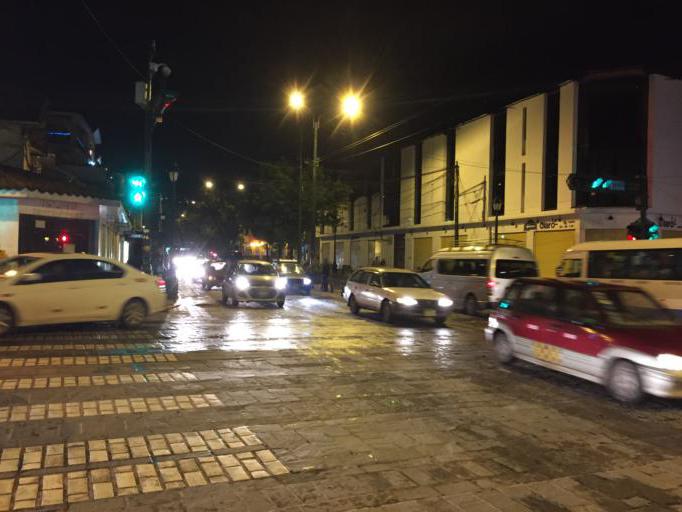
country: PE
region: Cusco
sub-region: Provincia de Cusco
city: Cusco
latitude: -13.5230
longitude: -71.9745
